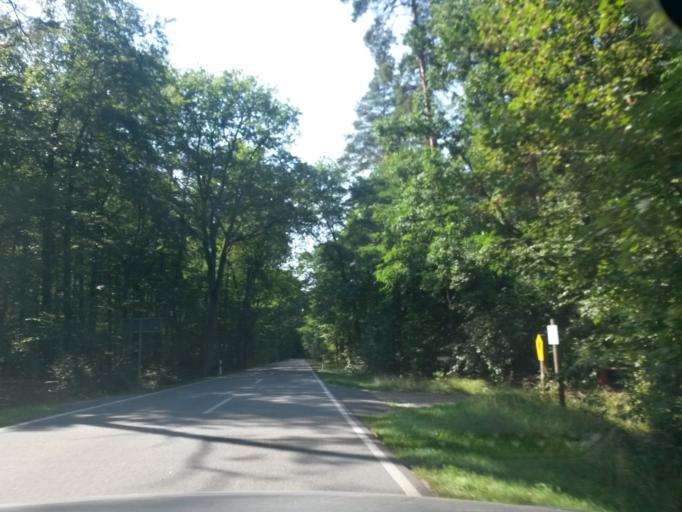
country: DE
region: Brandenburg
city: Marienwerder
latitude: 52.9000
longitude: 13.6433
